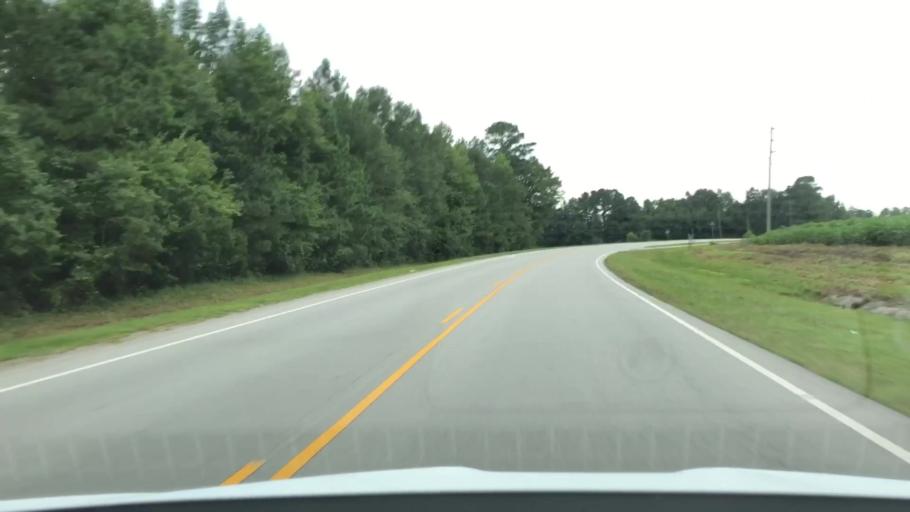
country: US
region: North Carolina
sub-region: Jones County
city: Trenton
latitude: 35.0397
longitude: -77.3487
